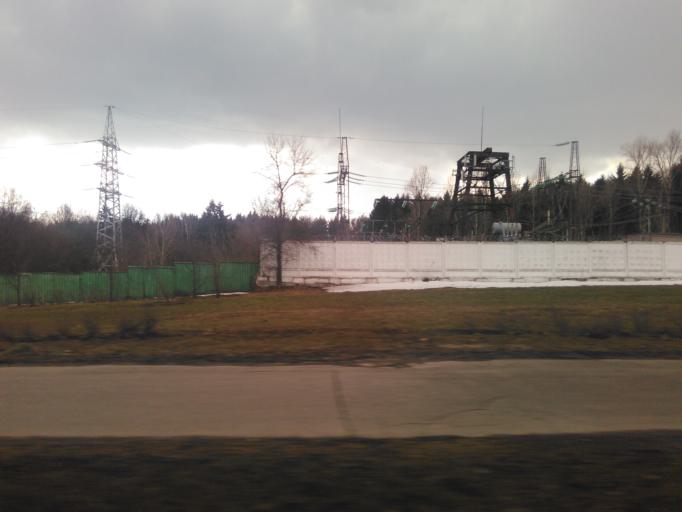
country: RU
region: Moscow
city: Zyuzino
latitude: 55.6484
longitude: 37.5683
